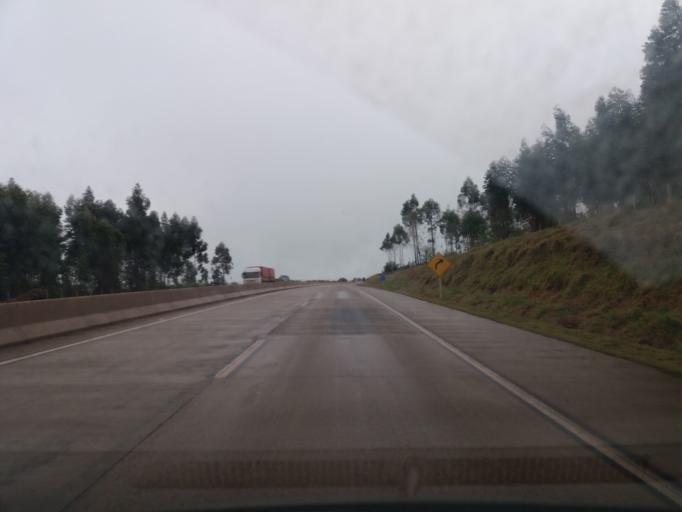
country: BR
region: Parana
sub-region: Cascavel
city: Cascavel
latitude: -25.1409
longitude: -53.5905
